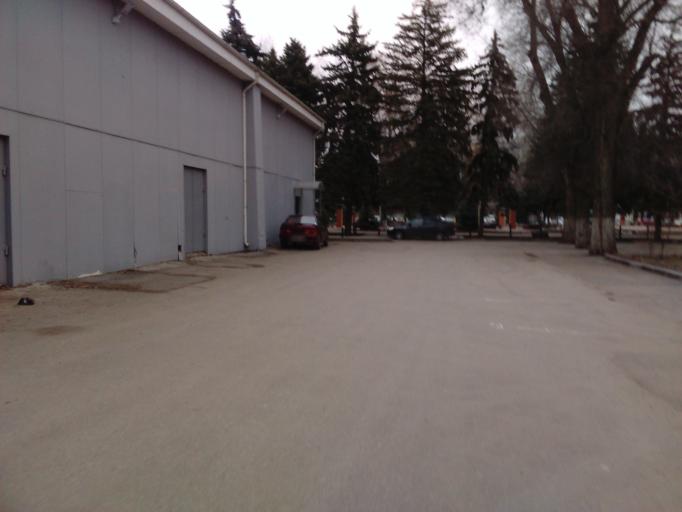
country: RU
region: Rostov
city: Bataysk
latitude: 47.1366
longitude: 39.7435
